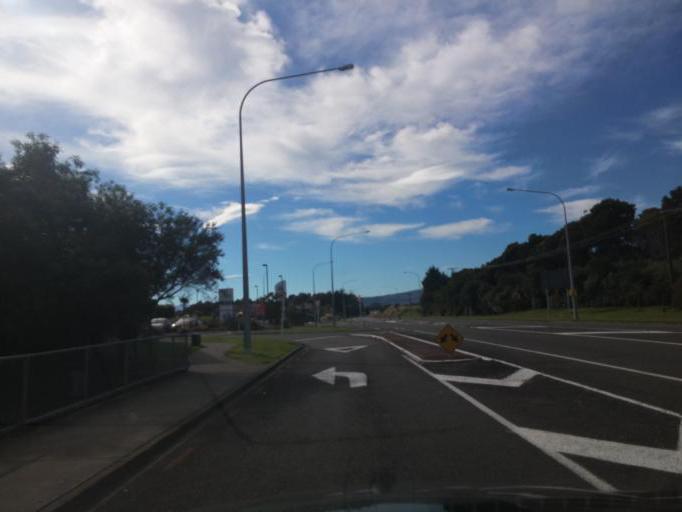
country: NZ
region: Manawatu-Wanganui
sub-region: Palmerston North City
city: Palmerston North
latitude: -40.3880
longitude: 175.6382
